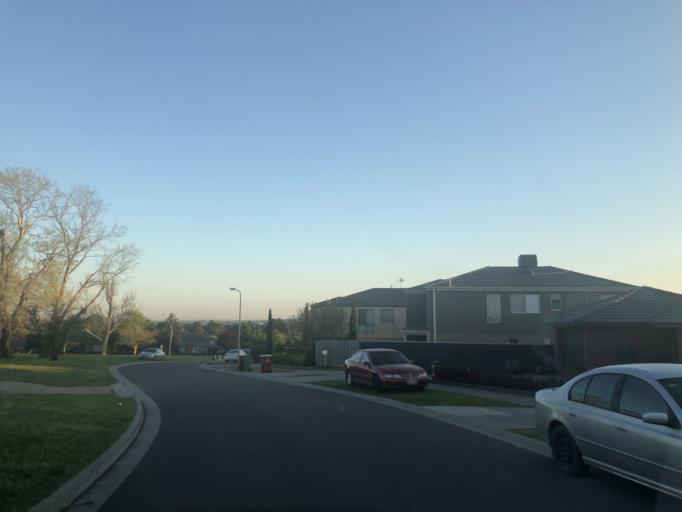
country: AU
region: Victoria
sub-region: Casey
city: Lynbrook
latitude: -38.0432
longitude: 145.2607
